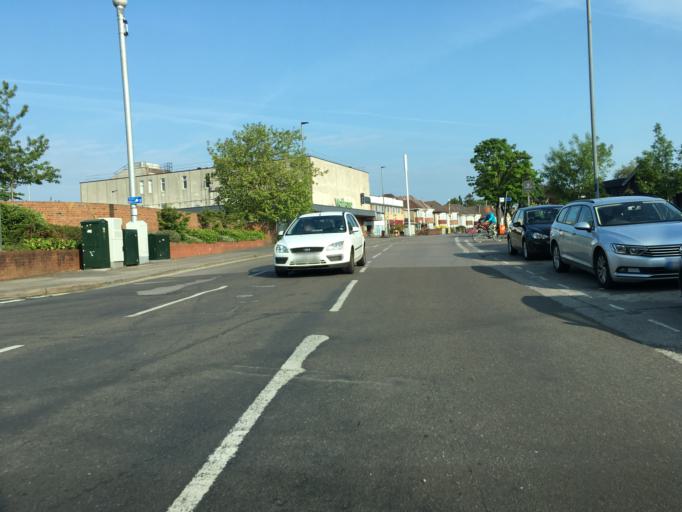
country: GB
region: England
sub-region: Bristol
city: Bristol
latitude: 51.4800
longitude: -2.6111
